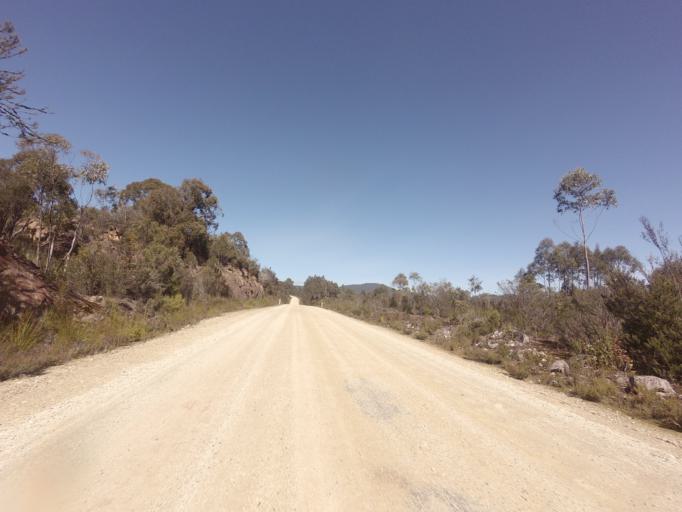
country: AU
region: Tasmania
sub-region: Huon Valley
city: Geeveston
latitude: -42.9066
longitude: 146.3681
